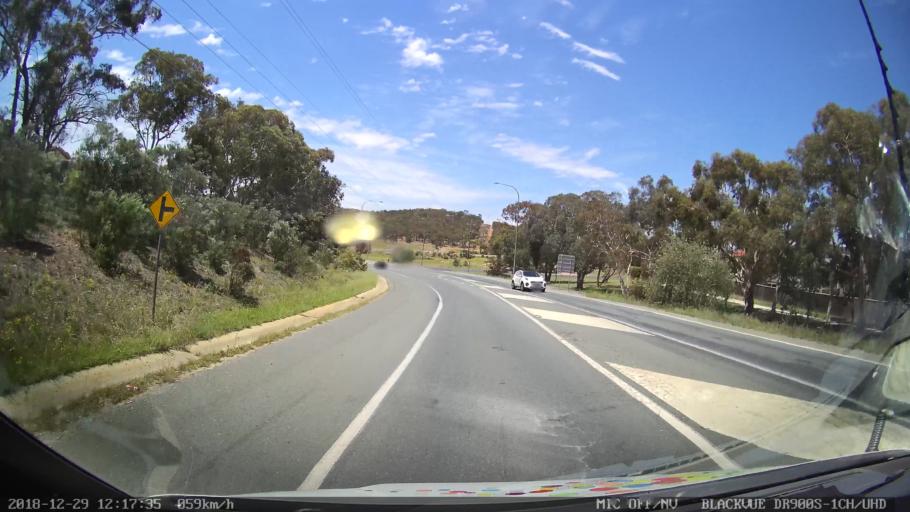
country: AU
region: New South Wales
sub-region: Queanbeyan
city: Queanbeyan
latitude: -35.3765
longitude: 149.2337
